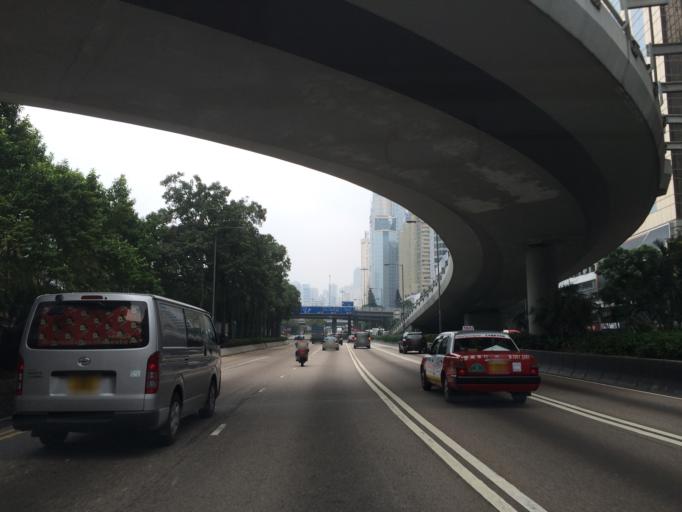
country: HK
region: Wanchai
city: Wan Chai
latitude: 22.2800
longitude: 114.1776
